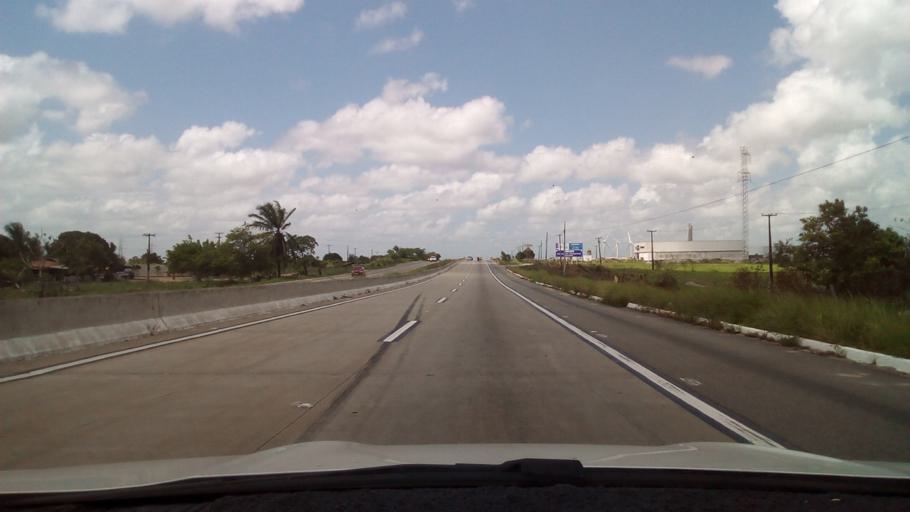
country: BR
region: Paraiba
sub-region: Conde
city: Conde
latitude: -7.2882
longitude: -34.9384
